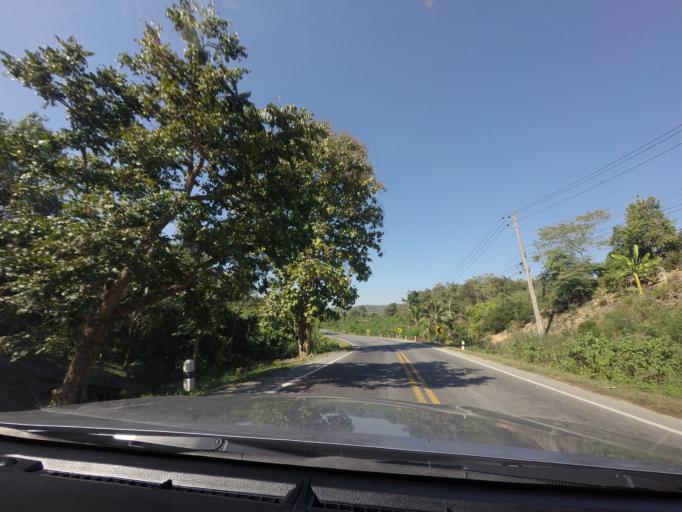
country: TH
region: Sukhothai
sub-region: Amphoe Si Satchanalai
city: Si Satchanalai
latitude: 17.6251
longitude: 99.7018
